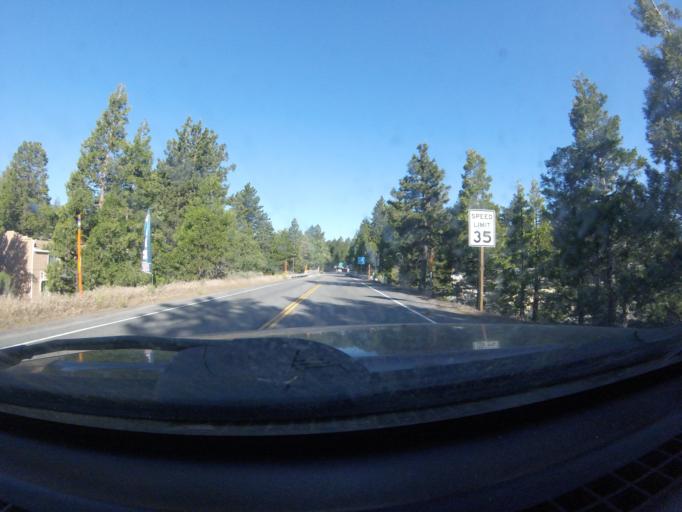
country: US
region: California
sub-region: San Bernardino County
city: Running Springs
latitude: 34.2051
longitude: -117.1053
